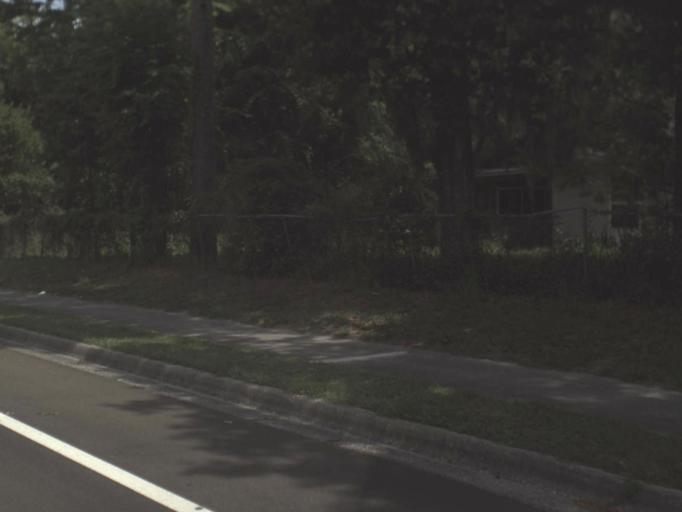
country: US
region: Florida
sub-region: Alachua County
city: Gainesville
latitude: 29.6316
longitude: -82.2658
